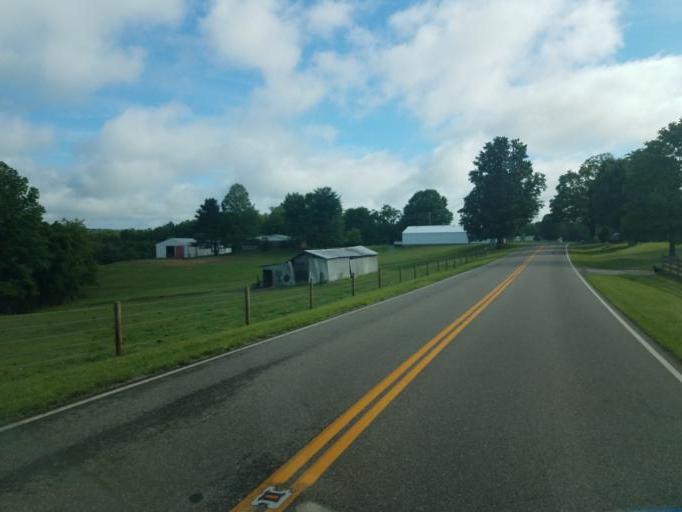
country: US
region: Ohio
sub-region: Jackson County
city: Oak Hill
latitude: 38.8509
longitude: -82.3892
